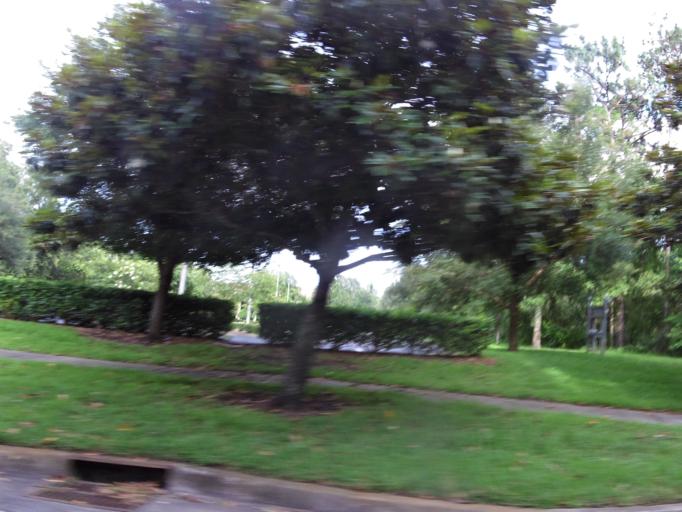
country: US
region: Florida
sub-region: Saint Johns County
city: Fruit Cove
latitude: 30.1818
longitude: -81.5498
